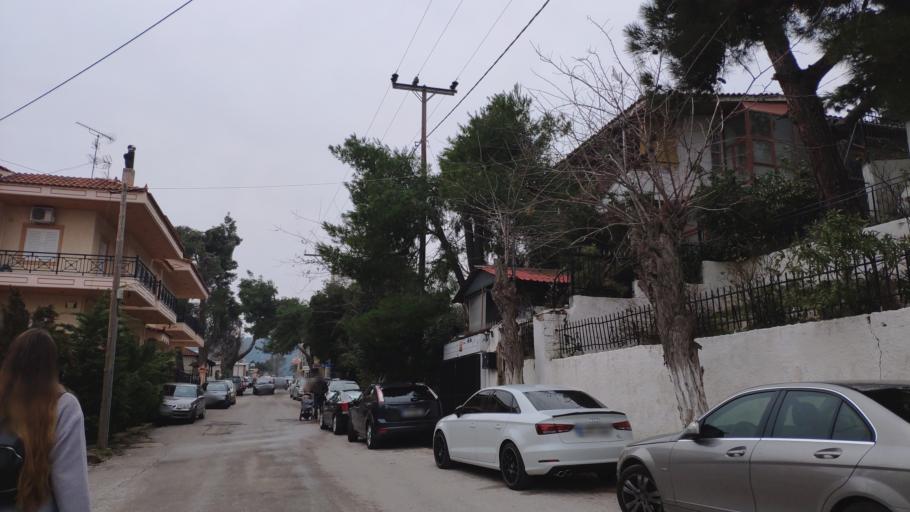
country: GR
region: Attica
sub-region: Nomarchia Dytikis Attikis
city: Vilia
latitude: 38.1671
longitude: 23.3331
